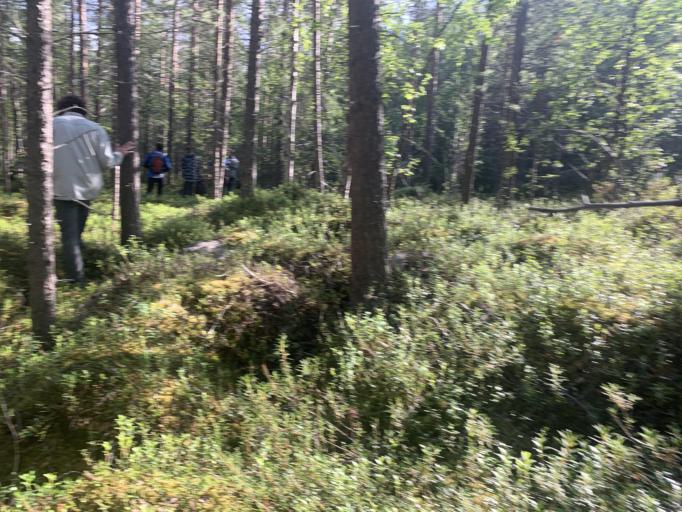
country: RU
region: Murmansk
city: Monchegorsk
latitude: 67.8798
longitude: 33.1049
